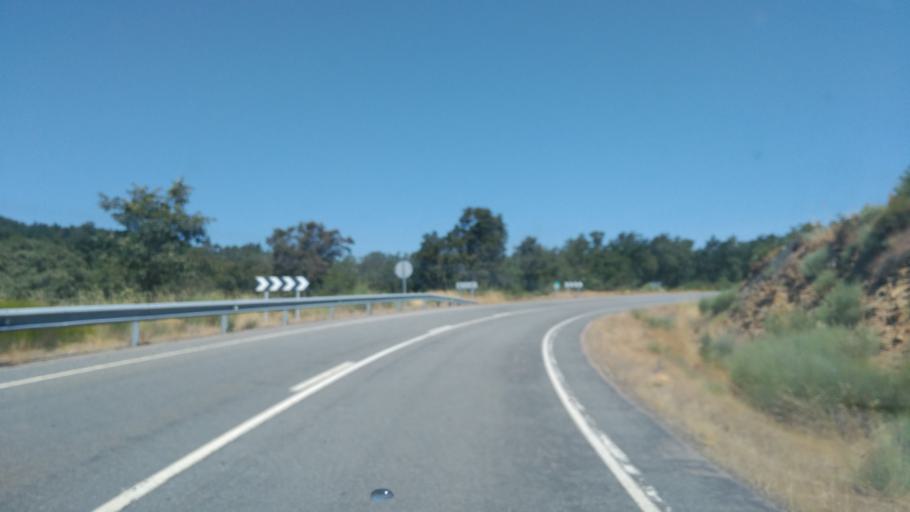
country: ES
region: Castille and Leon
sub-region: Provincia de Salamanca
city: Cereceda de la Sierra
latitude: 40.5890
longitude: -6.0890
